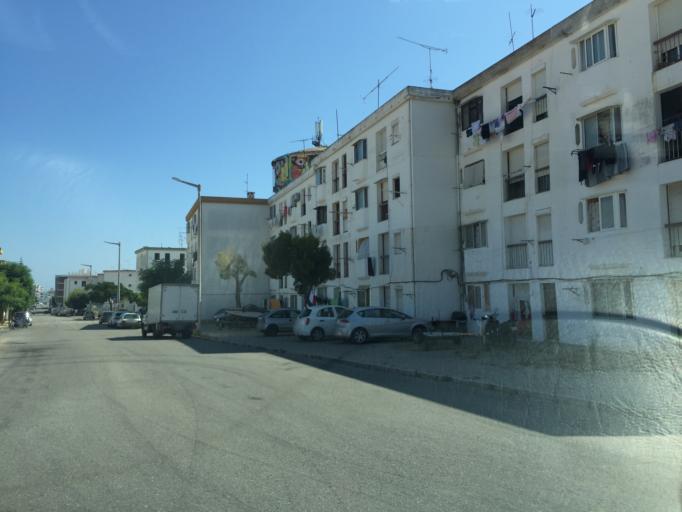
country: PT
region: Faro
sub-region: Olhao
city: Olhao
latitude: 37.0350
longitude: -7.8454
